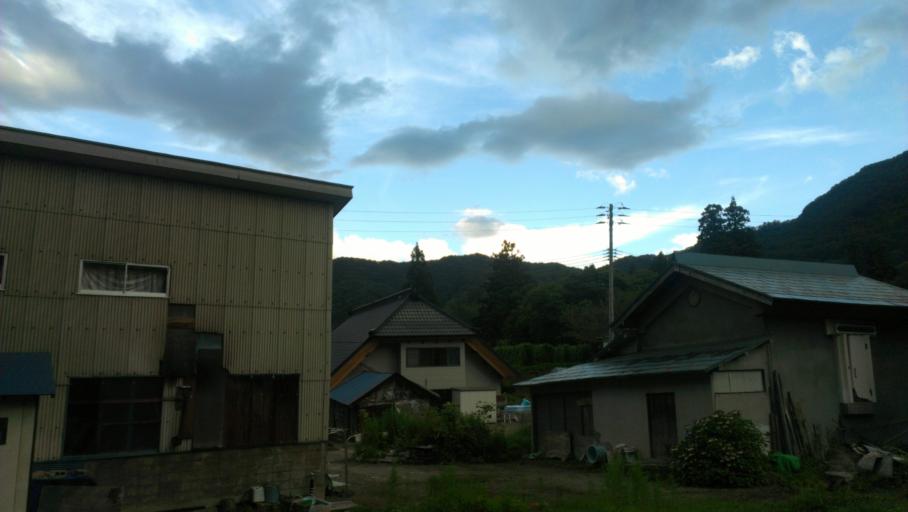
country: JP
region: Fukushima
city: Inawashiro
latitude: 37.4022
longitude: 139.9718
